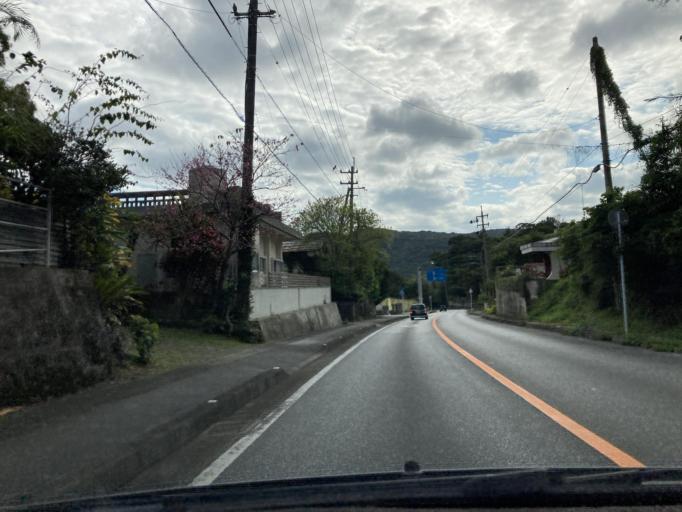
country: JP
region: Okinawa
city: Nago
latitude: 26.6562
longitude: 127.9838
